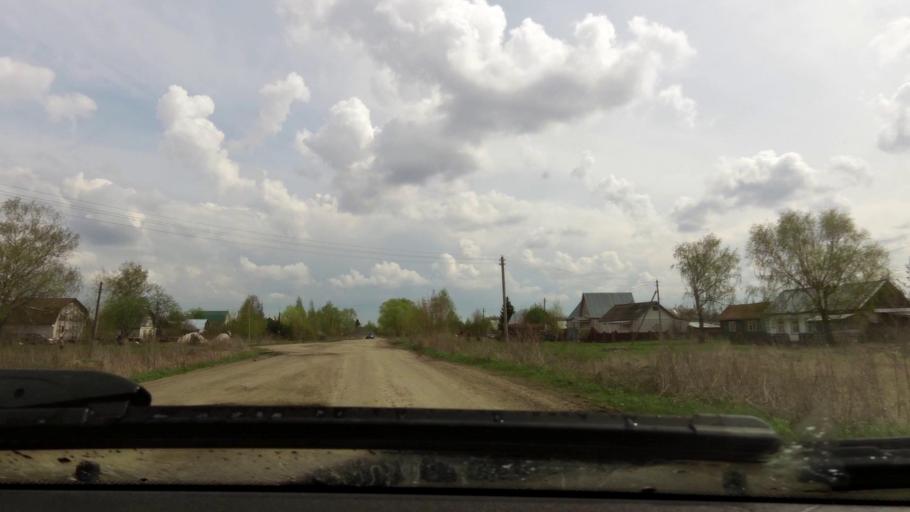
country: RU
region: Rjazan
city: Bagramovo
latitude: 54.6987
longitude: 39.3043
